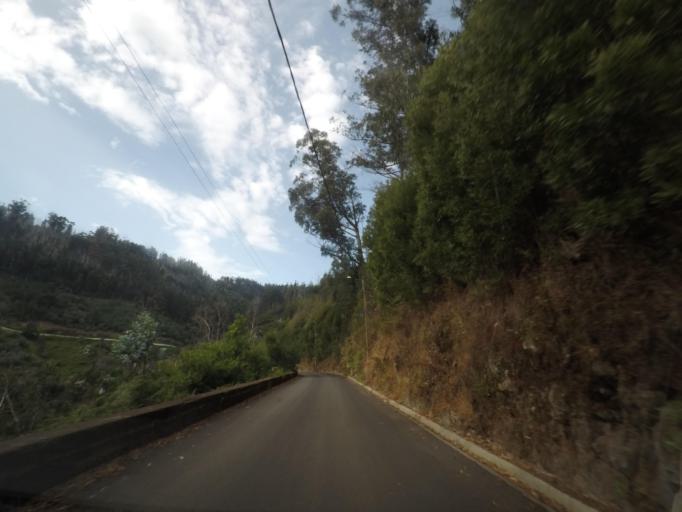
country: PT
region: Madeira
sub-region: Calheta
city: Arco da Calheta
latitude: 32.7420
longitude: -17.1531
